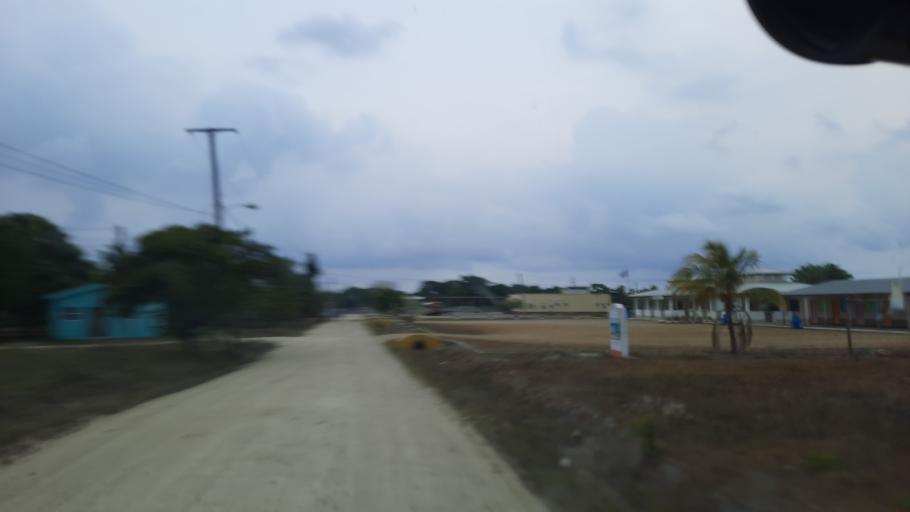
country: BZ
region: Stann Creek
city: Placencia
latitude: 16.5334
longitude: -88.4241
